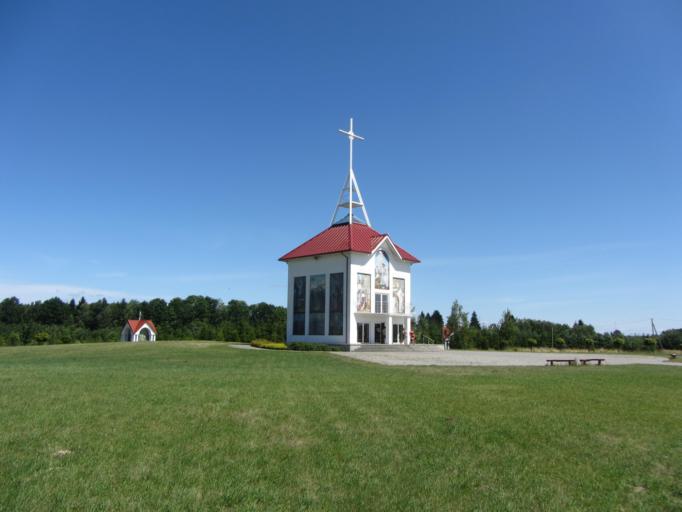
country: LT
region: Vilnius County
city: Elektrenai
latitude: 54.8404
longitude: 24.5659
